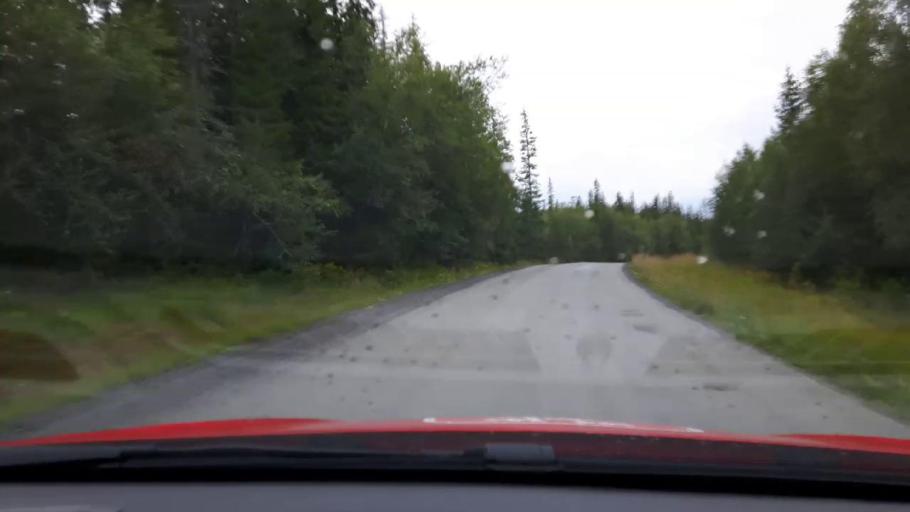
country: SE
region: Jaemtland
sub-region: Are Kommun
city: Are
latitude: 63.4518
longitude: 13.2085
